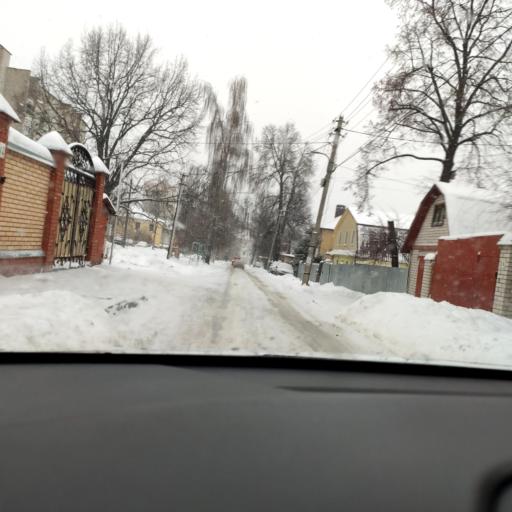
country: RU
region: Tatarstan
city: Vysokaya Gora
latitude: 55.8651
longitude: 49.2327
